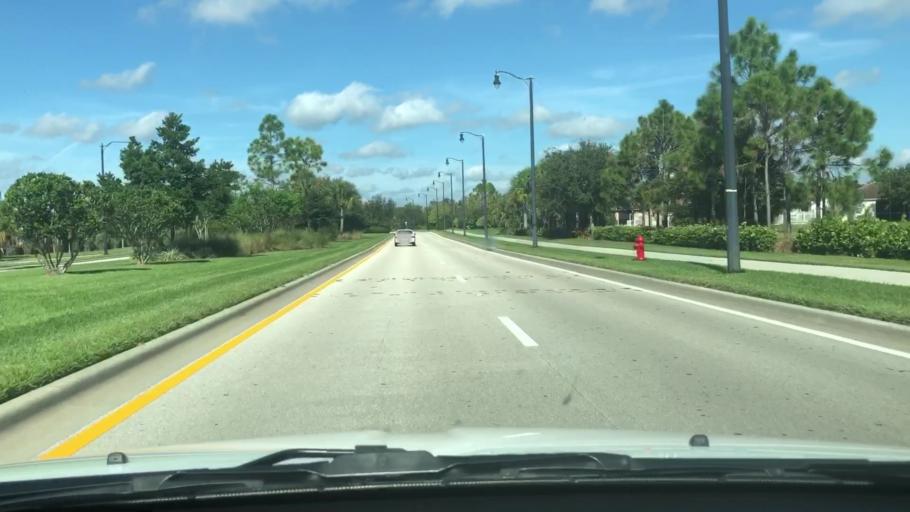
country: US
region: Florida
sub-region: Saint Lucie County
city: Port Saint Lucie
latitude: 27.2890
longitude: -80.4384
